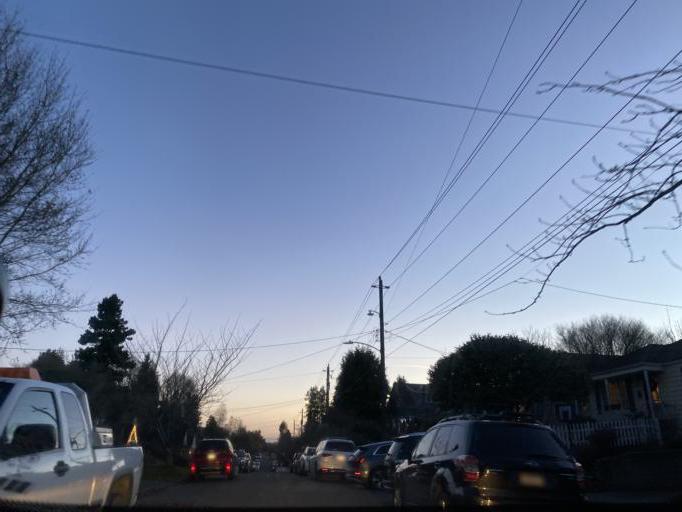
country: US
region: Washington
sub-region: King County
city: Seattle
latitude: 47.6573
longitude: -122.3995
